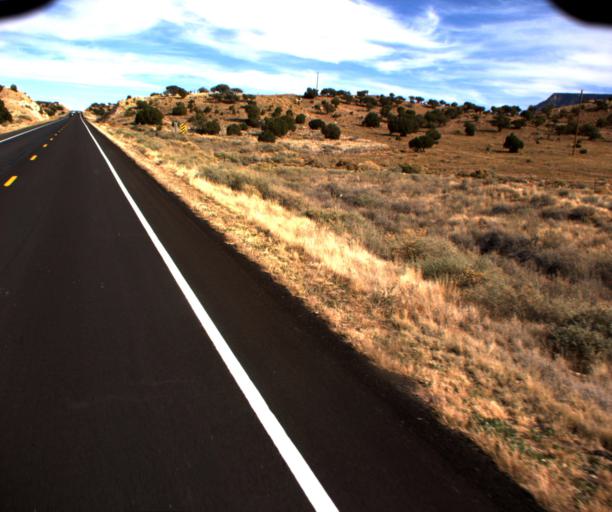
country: US
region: Arizona
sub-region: Navajo County
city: Kayenta
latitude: 36.6986
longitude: -110.3303
